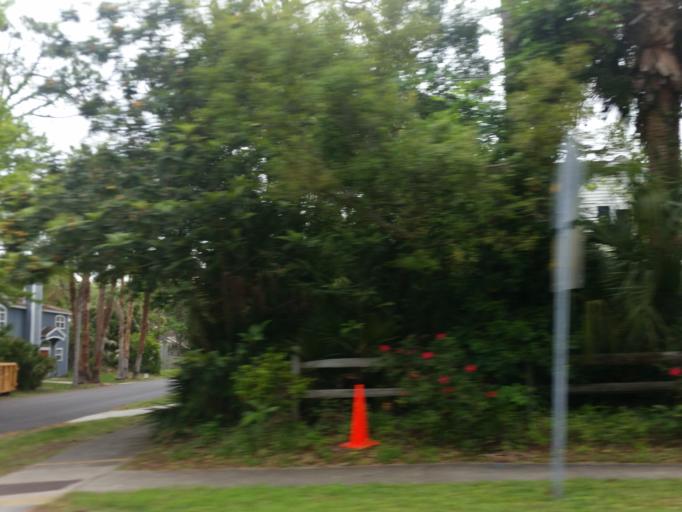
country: US
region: Florida
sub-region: Duval County
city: Atlantic Beach
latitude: 30.3288
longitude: -81.4041
